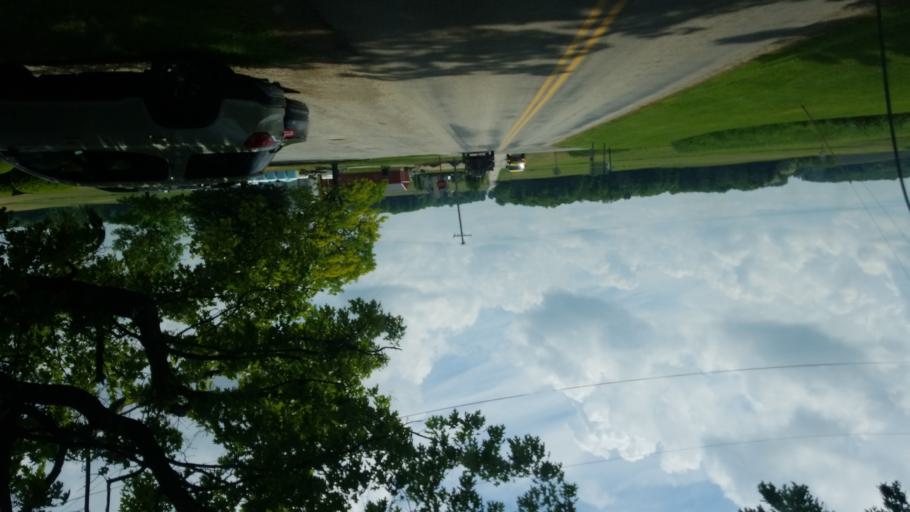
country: US
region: Ohio
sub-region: Ashland County
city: Ashland
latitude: 40.8060
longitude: -82.3047
